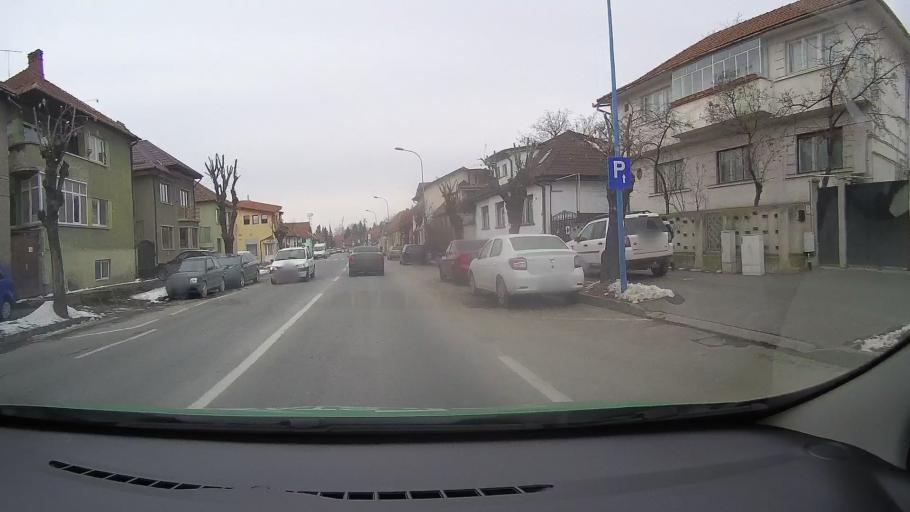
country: RO
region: Brasov
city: Brasov
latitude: 45.6596
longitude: 25.5920
